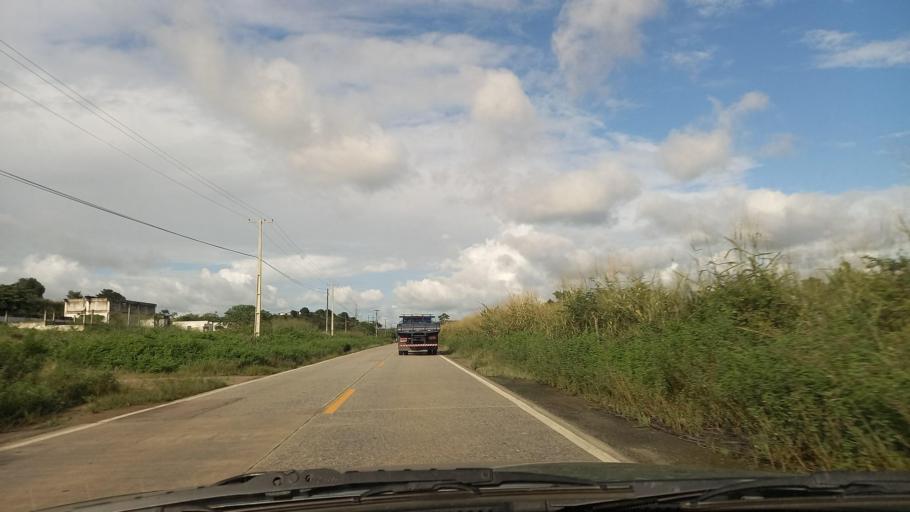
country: BR
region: Pernambuco
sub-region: Palmares
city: Palmares
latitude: -8.6914
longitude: -35.6244
